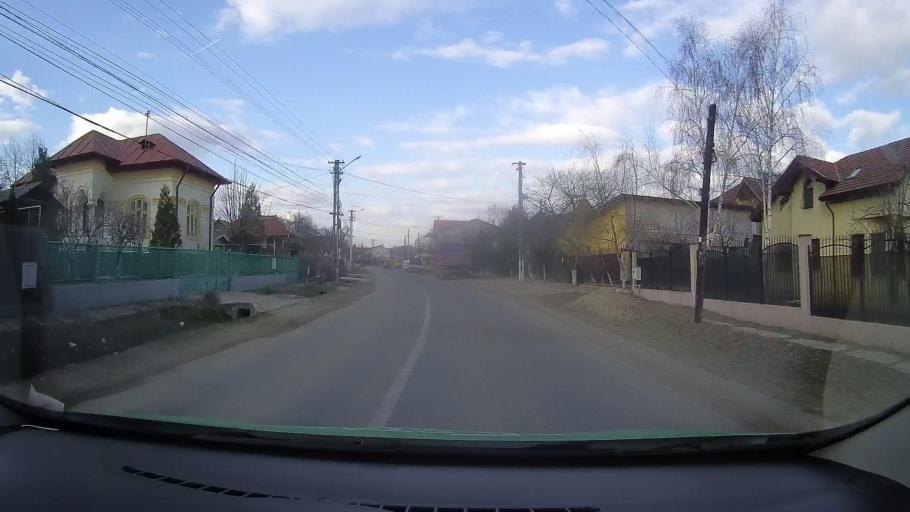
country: RO
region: Dambovita
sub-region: Comuna Gura Ocnitei
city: Gura Ocnitei
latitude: 44.9340
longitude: 25.5620
